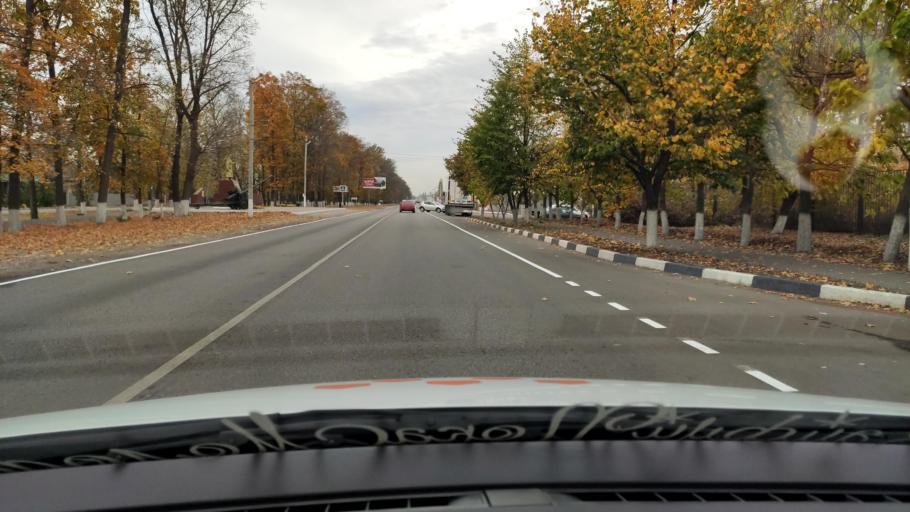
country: RU
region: Voronezj
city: Ramon'
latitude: 51.9106
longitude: 39.3298
